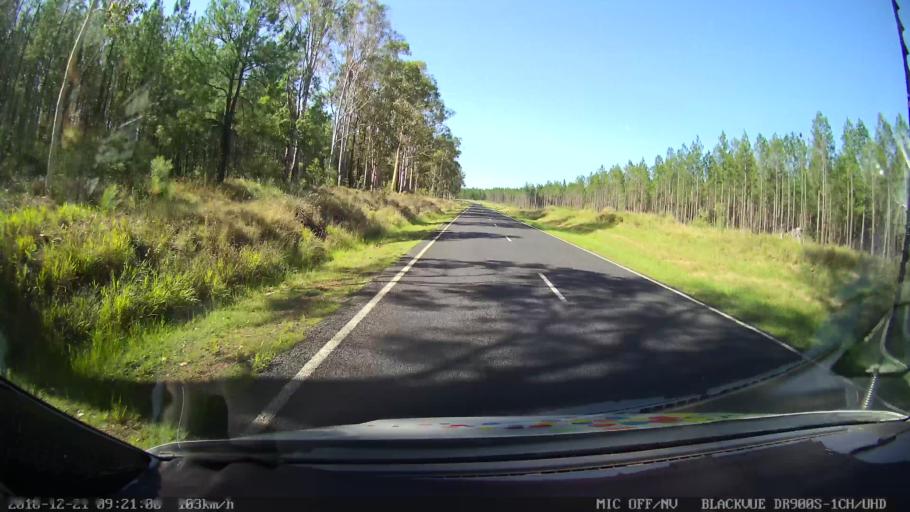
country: AU
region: New South Wales
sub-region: Clarence Valley
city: Maclean
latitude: -29.3228
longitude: 152.9988
